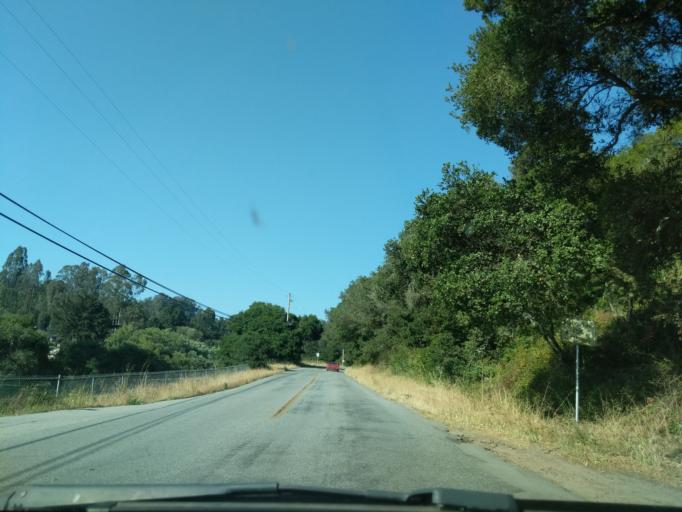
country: US
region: California
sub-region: Monterey County
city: Prunedale
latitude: 36.7943
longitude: -121.6591
